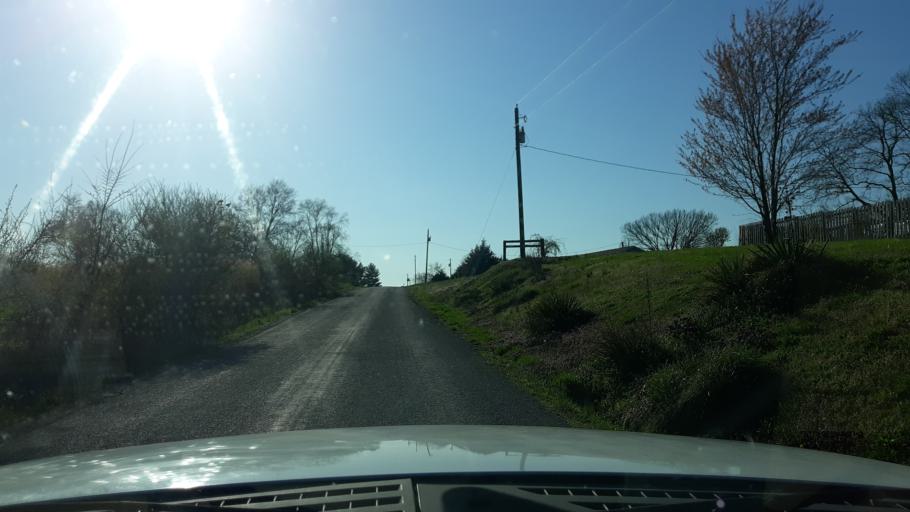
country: US
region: Illinois
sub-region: Saline County
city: Harrisburg
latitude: 37.7753
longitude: -88.5947
